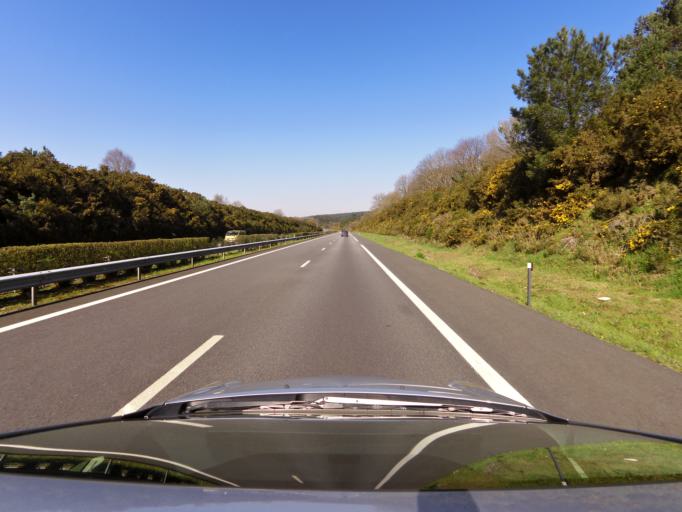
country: FR
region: Brittany
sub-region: Departement du Morbihan
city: Beignon
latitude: 47.9268
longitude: -2.1850
